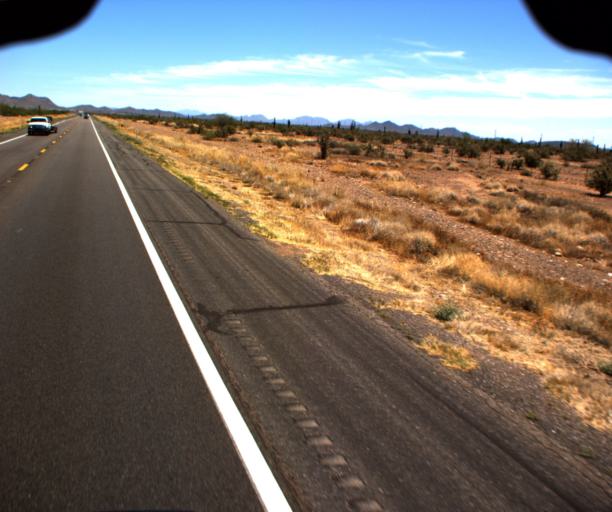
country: US
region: Arizona
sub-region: Maricopa County
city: Anthem
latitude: 33.7978
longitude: -112.1948
